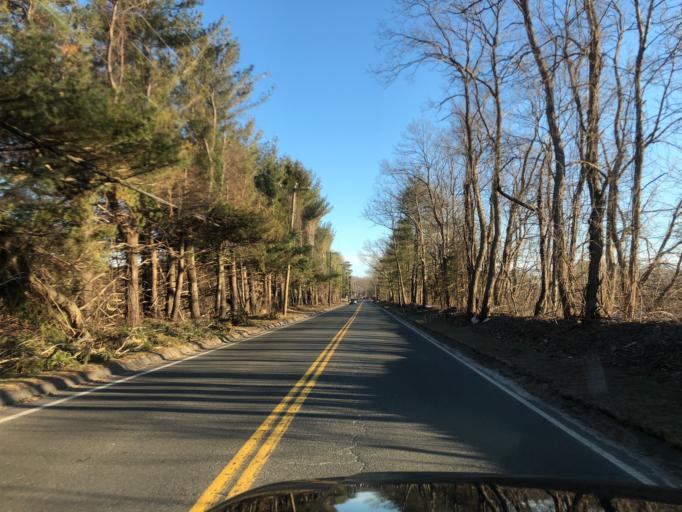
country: US
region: Connecticut
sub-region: Hartford County
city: Farmington
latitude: 41.7450
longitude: -72.8537
